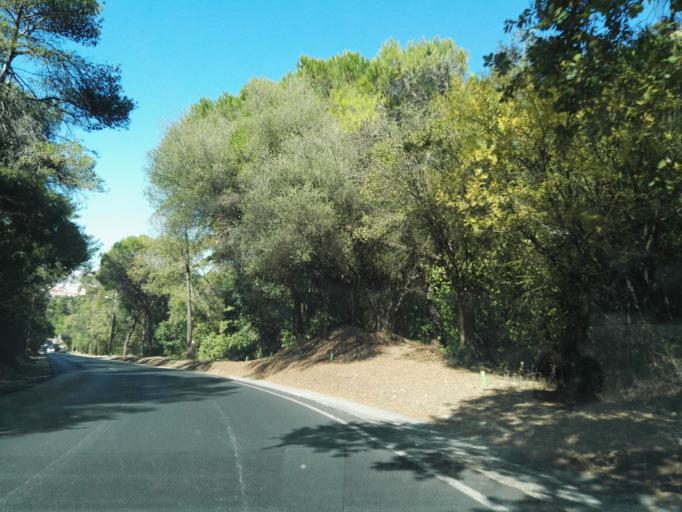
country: PT
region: Lisbon
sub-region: Odivelas
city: Pontinha
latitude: 38.7332
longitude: -9.1980
